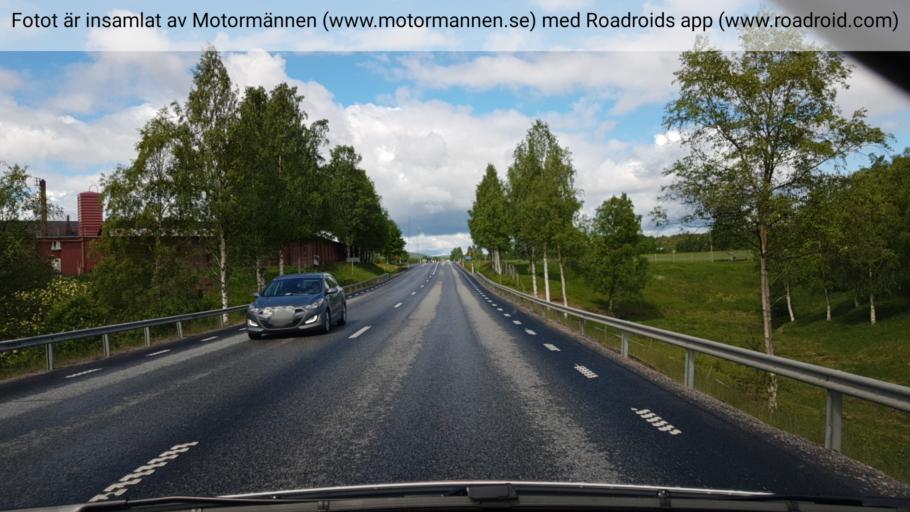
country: SE
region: Vaesterbotten
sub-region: Umea Kommun
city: Roback
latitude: 63.8725
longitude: 20.0690
